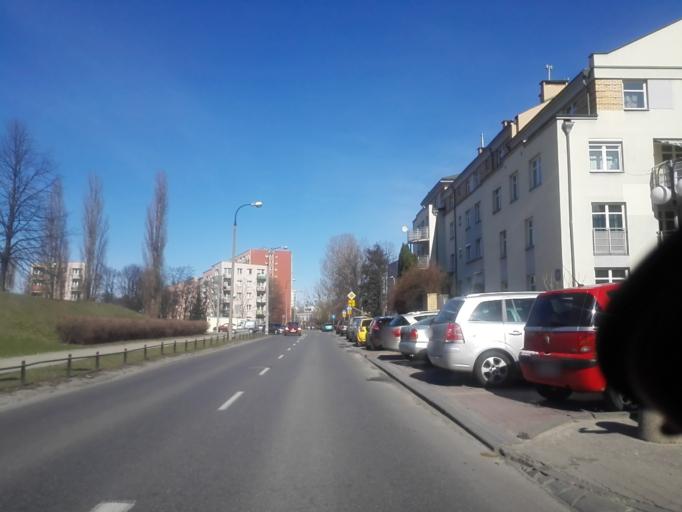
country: PL
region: Masovian Voivodeship
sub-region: Warszawa
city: Ochota
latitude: 52.1994
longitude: 20.9791
